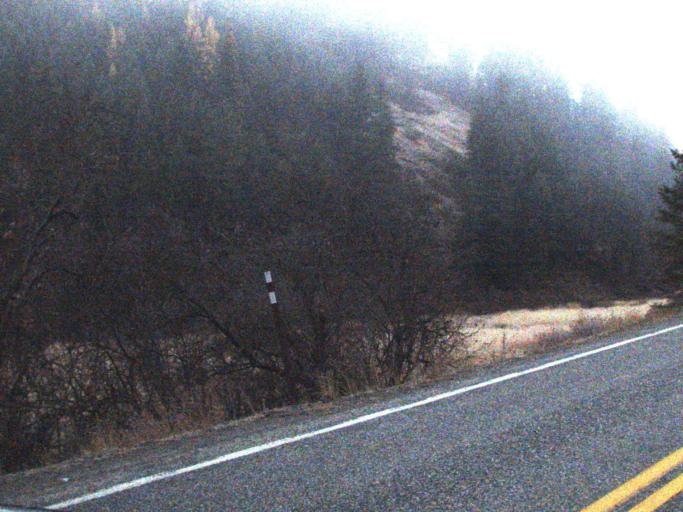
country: US
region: Washington
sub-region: Ferry County
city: Republic
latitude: 48.5513
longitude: -118.7463
